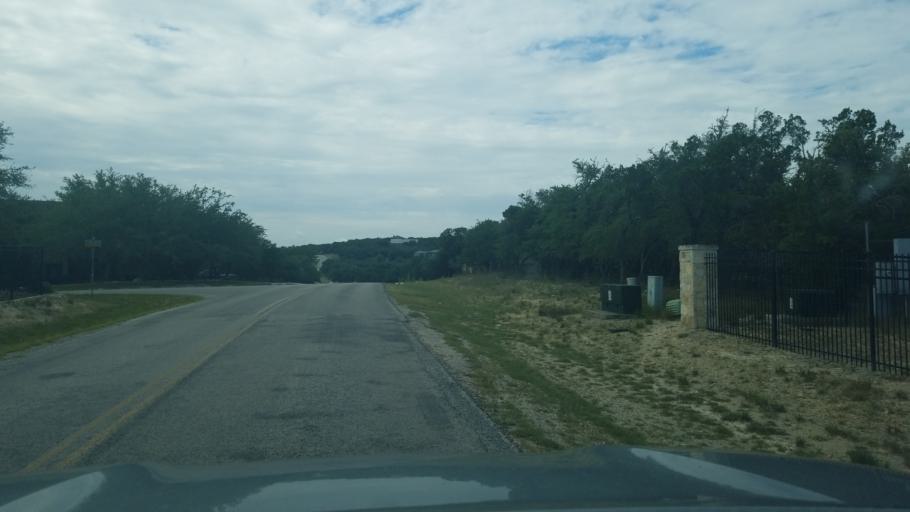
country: US
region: Texas
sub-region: Comal County
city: Bulverde
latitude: 29.8260
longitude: -98.4072
